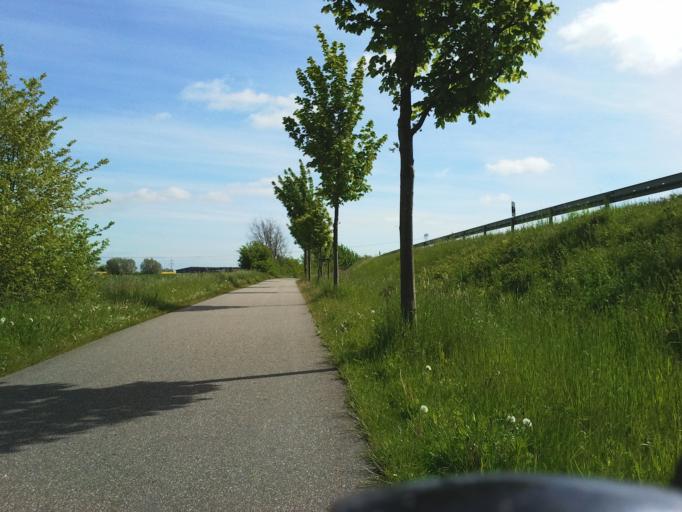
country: DE
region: Mecklenburg-Vorpommern
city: Papendorf
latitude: 54.0508
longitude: 12.1181
